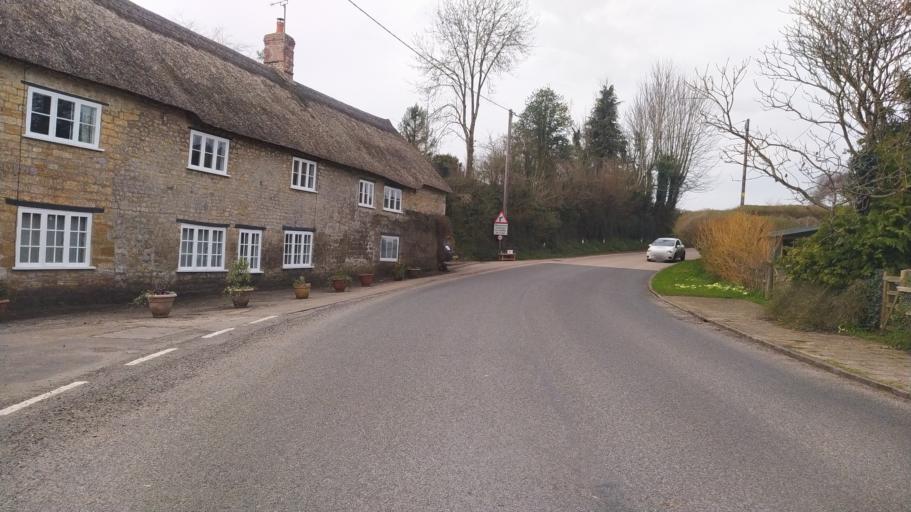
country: GB
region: England
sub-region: Somerset
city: Crewkerne
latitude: 50.8580
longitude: -2.7520
